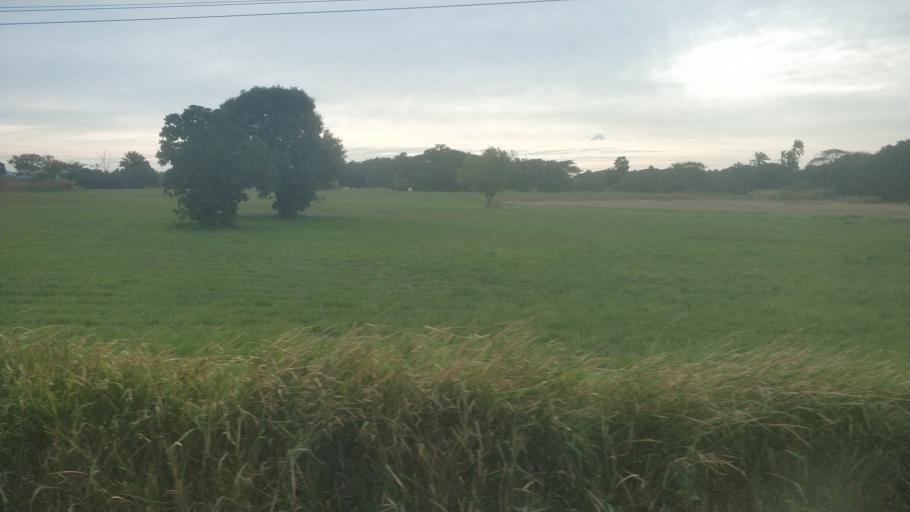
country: BR
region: Rio de Janeiro
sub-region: Seropedica
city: Seropedica
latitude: -22.7629
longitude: -43.6846
